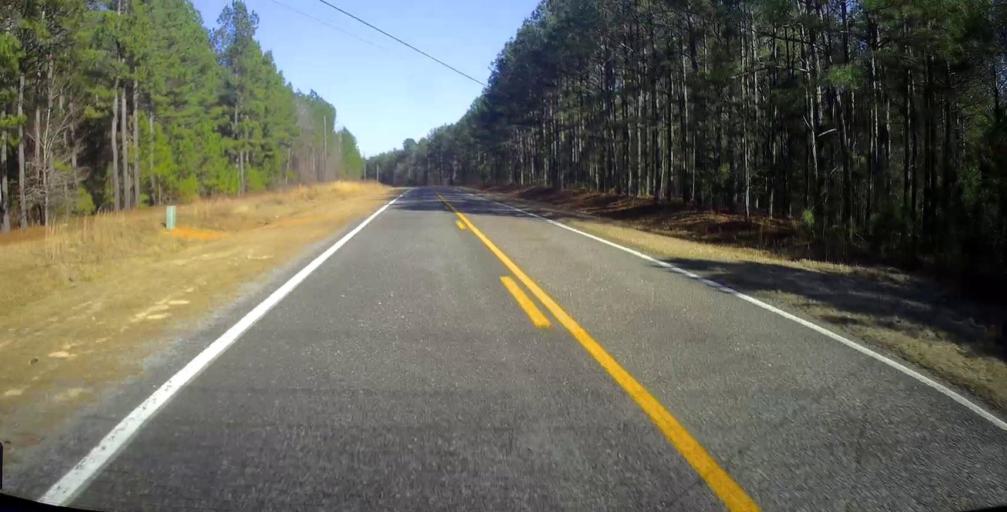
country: US
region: Georgia
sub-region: Peach County
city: Fort Valley
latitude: 32.6376
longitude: -83.9289
